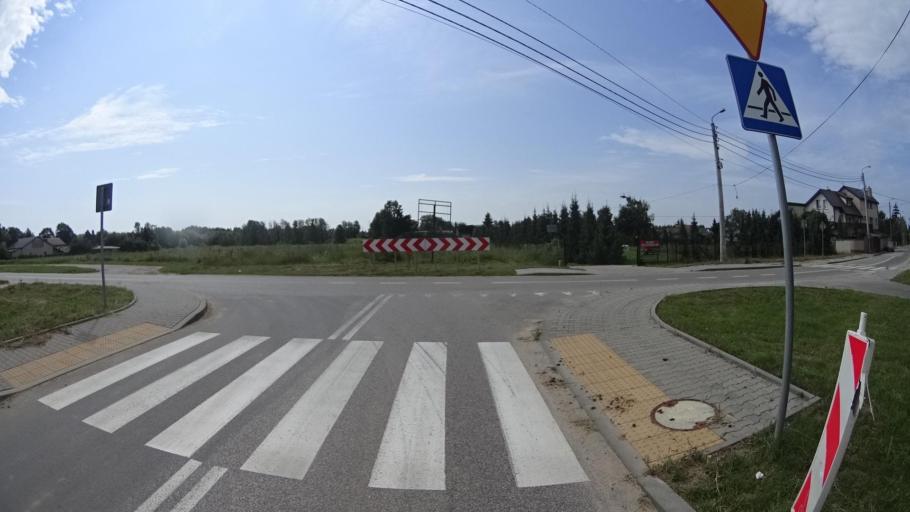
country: PL
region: Masovian Voivodeship
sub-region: Powiat pruszkowski
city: Nadarzyn
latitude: 52.0805
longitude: 20.7927
